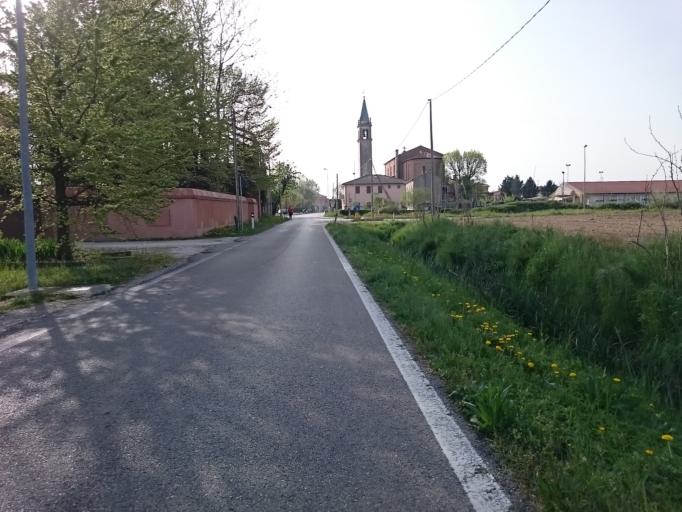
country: IT
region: Veneto
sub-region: Provincia di Padova
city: Masera di Padova
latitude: 45.3322
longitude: 11.8694
